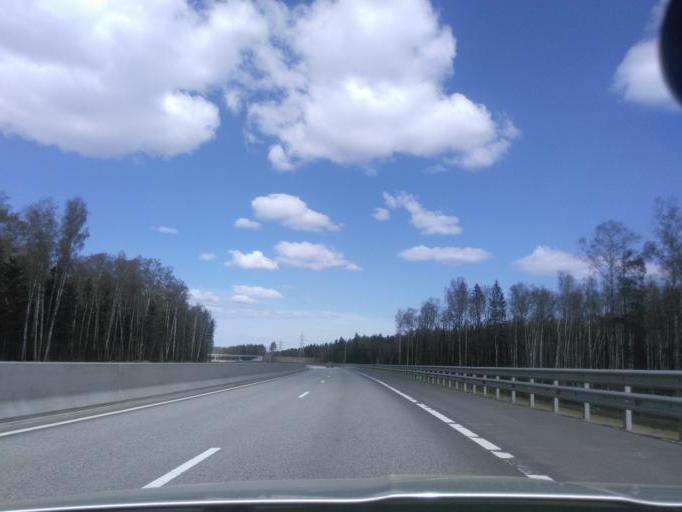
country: RU
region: Moskovskaya
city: Peshki
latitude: 56.1343
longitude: 37.1042
